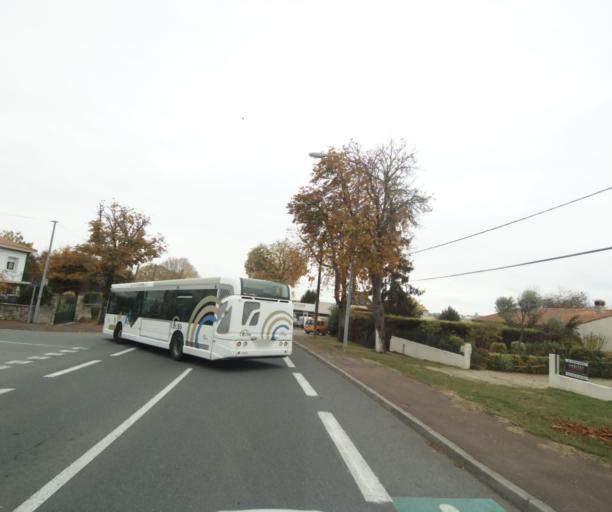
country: FR
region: Poitou-Charentes
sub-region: Departement de la Charente-Maritime
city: Saintes
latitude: 45.7317
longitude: -0.6456
